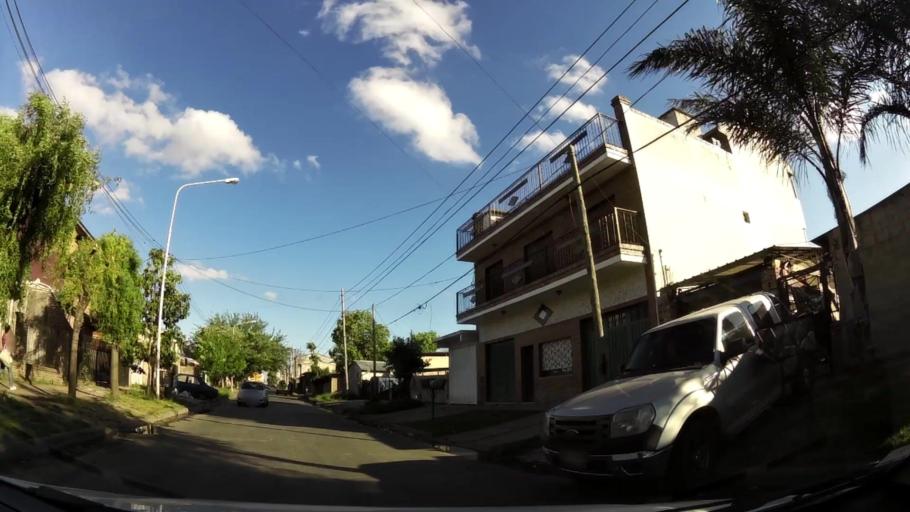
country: AR
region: Buenos Aires
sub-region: Partido de Moron
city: Moron
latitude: -34.6815
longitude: -58.6216
